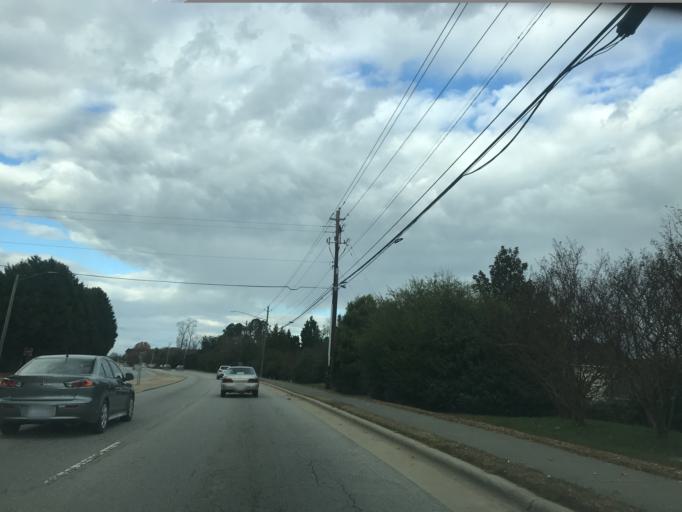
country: US
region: North Carolina
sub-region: Wake County
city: Raleigh
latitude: 35.8069
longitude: -78.5645
